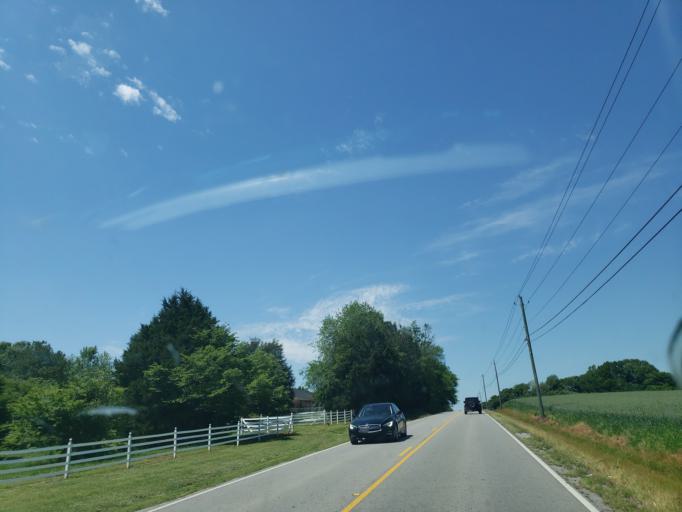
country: US
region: Alabama
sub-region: Madison County
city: Hazel Green
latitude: 34.9322
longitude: -86.5370
